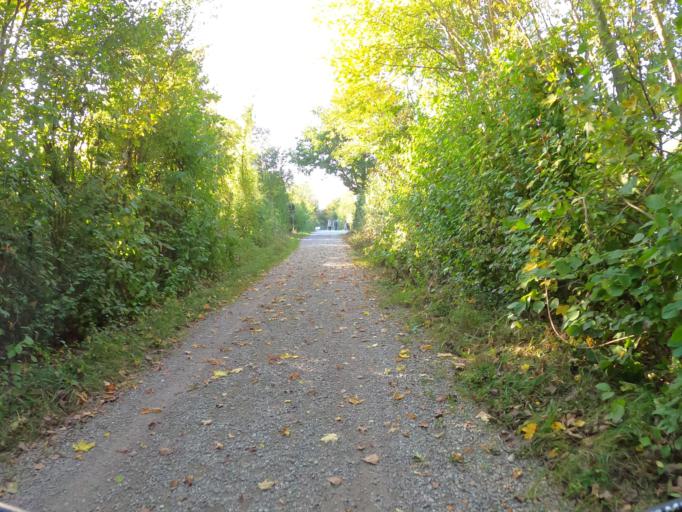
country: DE
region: Bavaria
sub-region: Swabia
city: Nersingen
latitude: 48.4465
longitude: 10.1282
